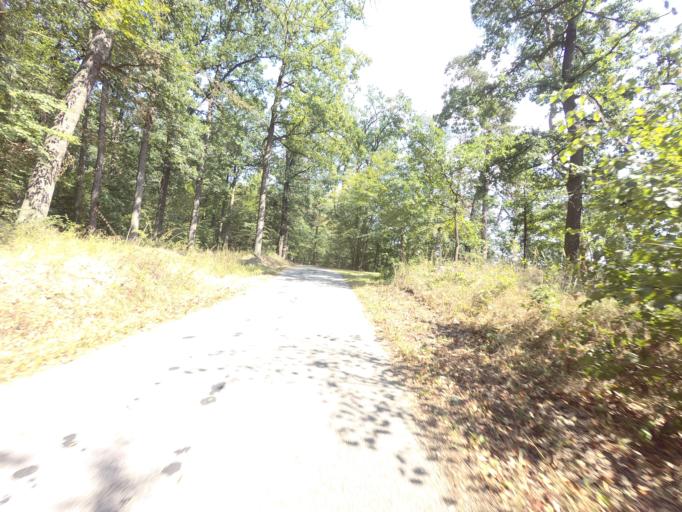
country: CZ
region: Jihocesky
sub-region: Okres Ceske Budejovice
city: Hluboka nad Vltavou
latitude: 49.0636
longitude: 14.4463
